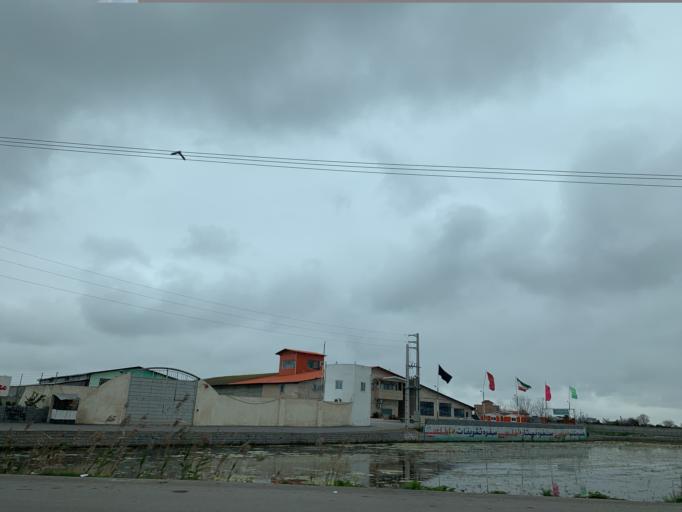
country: IR
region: Mazandaran
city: Babol
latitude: 36.5223
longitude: 52.6028
